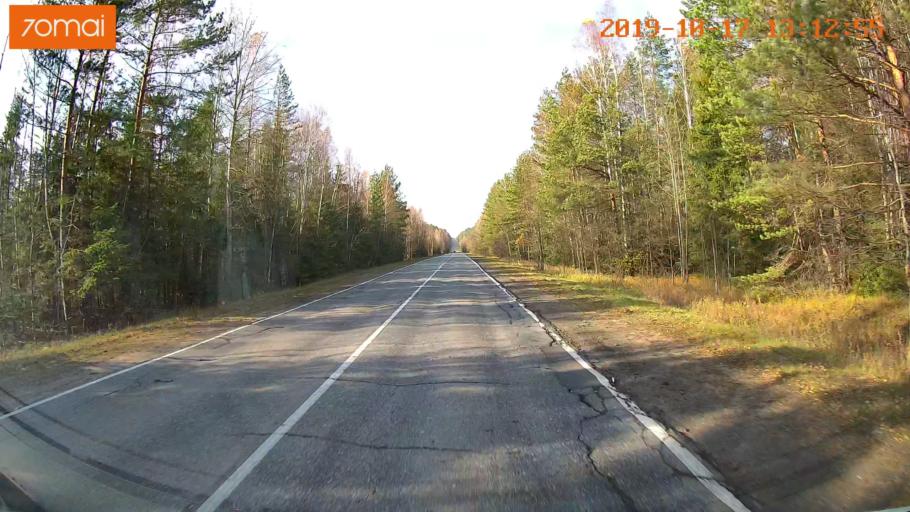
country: RU
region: Rjazan
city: Gus'-Zheleznyy
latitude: 55.0405
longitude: 41.2024
